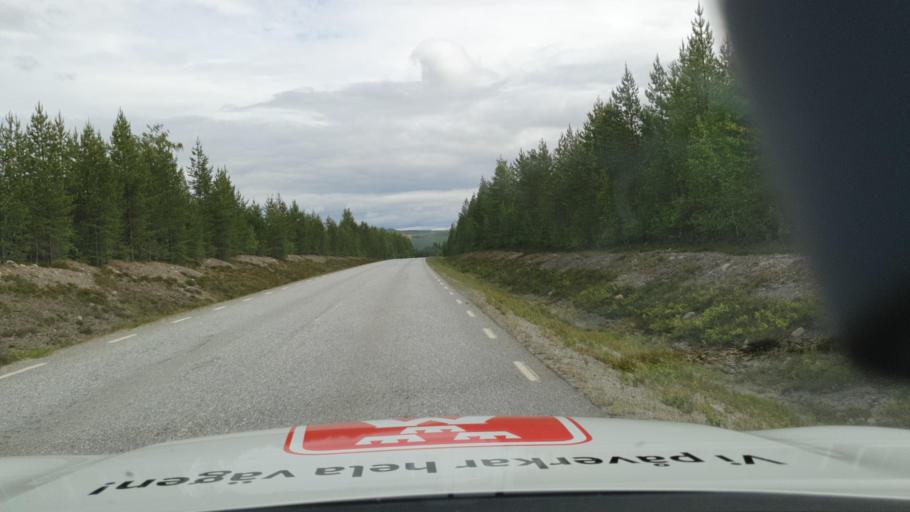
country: SE
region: Vaesterbotten
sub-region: Asele Kommun
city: Asele
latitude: 64.2160
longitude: 16.9047
